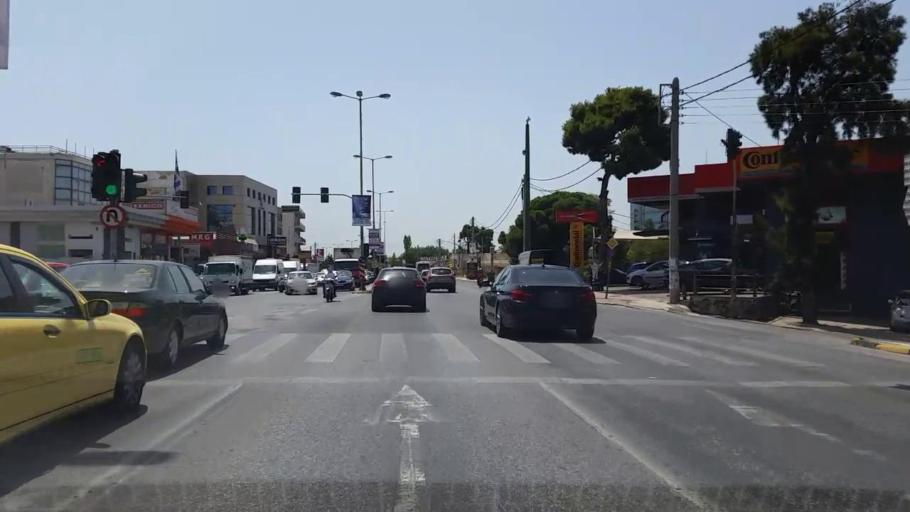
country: GR
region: Attica
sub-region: Nomarchia Athinas
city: Cholargos
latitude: 38.0114
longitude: 23.8118
